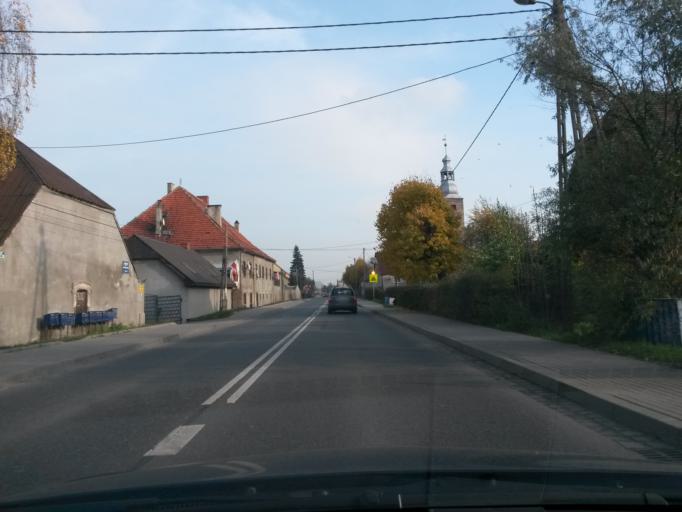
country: PL
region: Lower Silesian Voivodeship
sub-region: Powiat sredzki
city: Udanin
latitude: 50.9884
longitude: 16.4145
